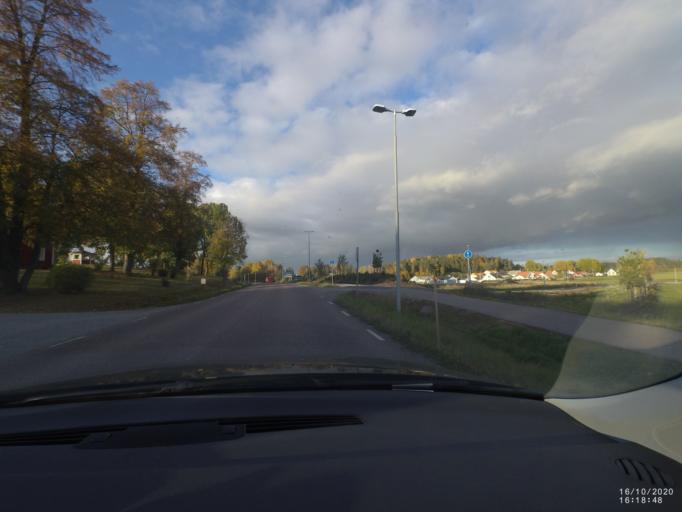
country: SE
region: Soedermanland
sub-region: Nykopings Kommun
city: Nykoping
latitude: 58.7720
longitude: 17.0068
